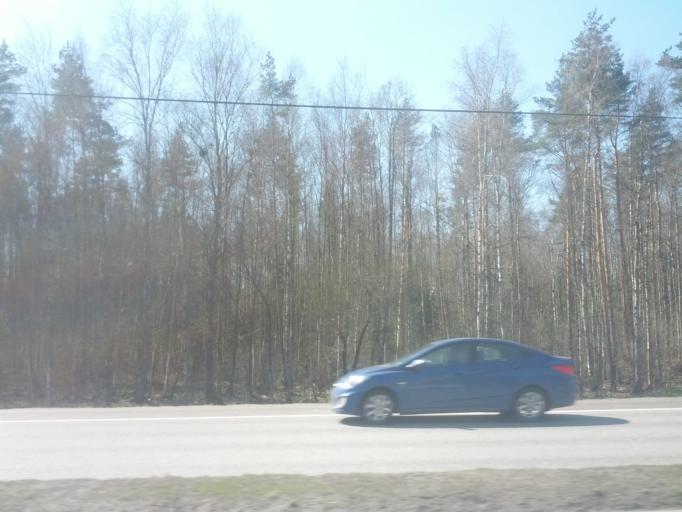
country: RU
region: St.-Petersburg
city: Razliv
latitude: 60.0741
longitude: 29.9661
